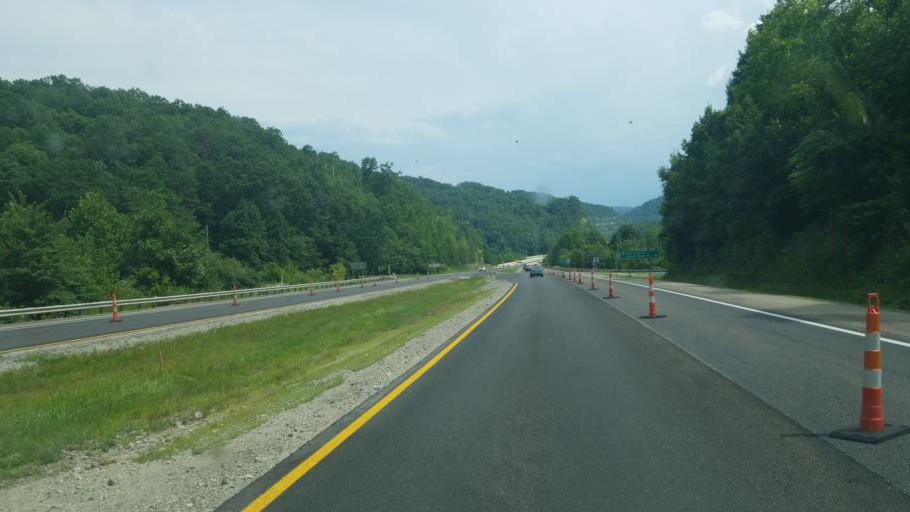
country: US
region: West Virginia
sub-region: Kanawha County
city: Alum Creek
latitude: 38.2281
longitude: -81.8383
